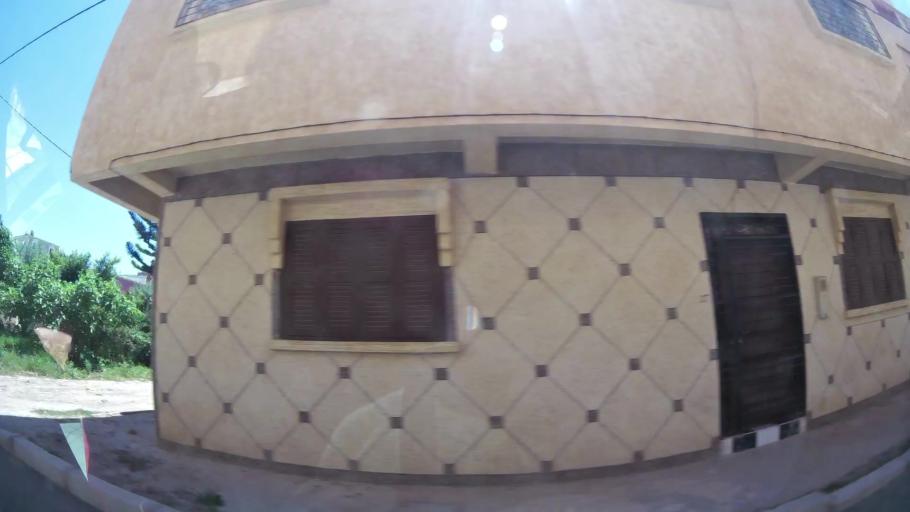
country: MA
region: Oriental
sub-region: Berkane-Taourirt
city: Madagh
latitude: 35.0764
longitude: -2.2188
